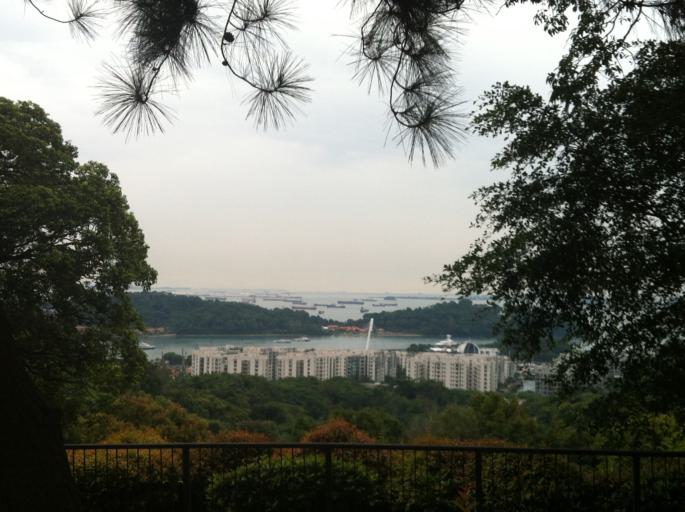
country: SG
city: Singapore
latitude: 1.2730
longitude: 103.8185
